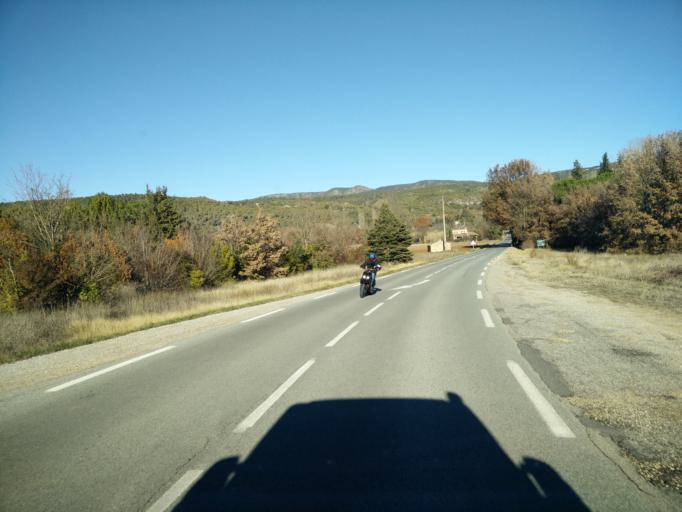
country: FR
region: Provence-Alpes-Cote d'Azur
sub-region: Departement du Var
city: Villecroze
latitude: 43.5709
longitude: 6.2609
